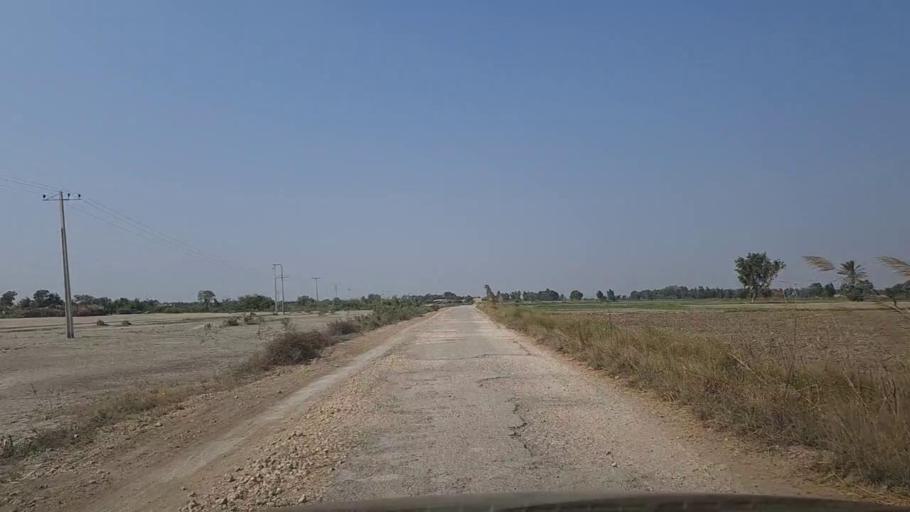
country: PK
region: Sindh
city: Mirpur Sakro
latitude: 24.6093
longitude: 67.7837
